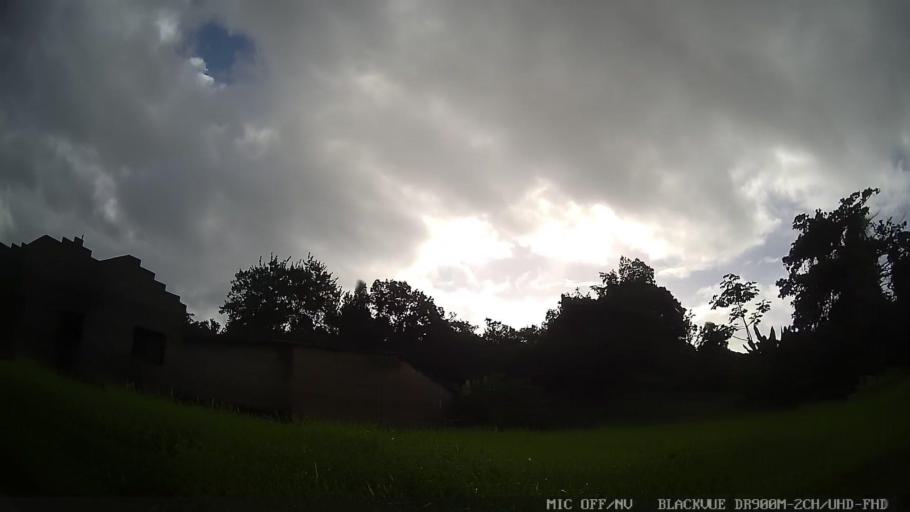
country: BR
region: Sao Paulo
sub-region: Itanhaem
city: Itanhaem
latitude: -24.1981
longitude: -46.8290
